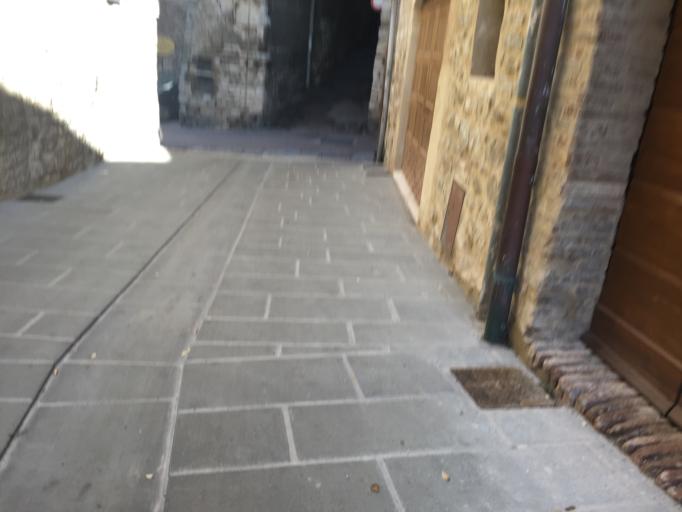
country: IT
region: Umbria
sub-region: Provincia di Perugia
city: Perugia
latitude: 43.1127
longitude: 12.3846
